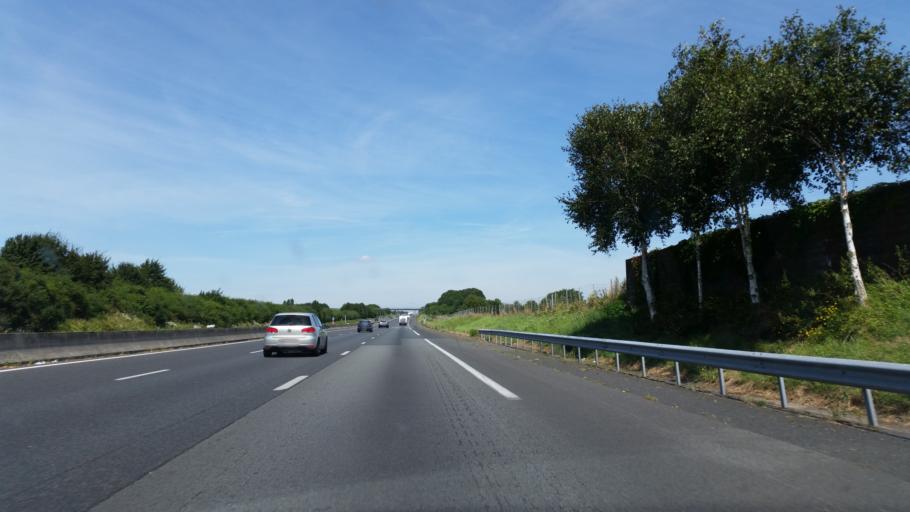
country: FR
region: Nord-Pas-de-Calais
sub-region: Departement du Pas-de-Calais
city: Bapaume
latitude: 50.1315
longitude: 2.8719
